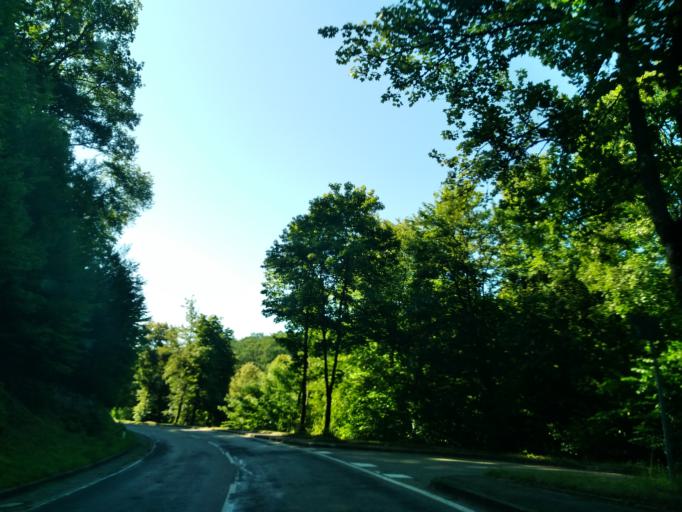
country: DE
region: Baden-Wuerttemberg
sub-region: Karlsruhe Region
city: Buchen
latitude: 49.5288
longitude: 9.3111
